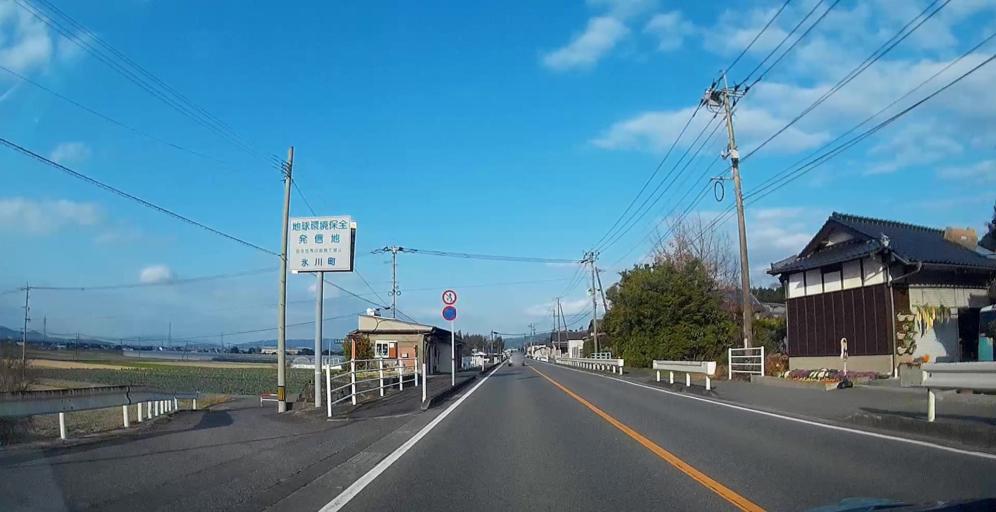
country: JP
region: Kumamoto
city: Matsubase
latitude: 32.5676
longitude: 130.6896
